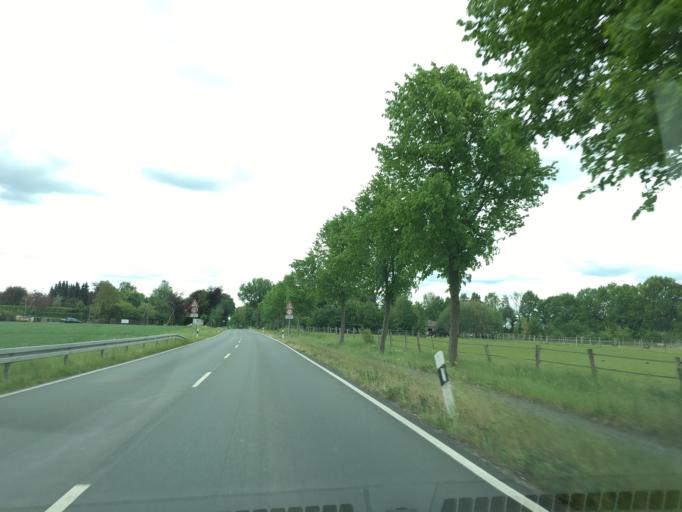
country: DE
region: North Rhine-Westphalia
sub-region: Regierungsbezirk Munster
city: Havixbeck
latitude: 51.9343
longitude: 7.4511
